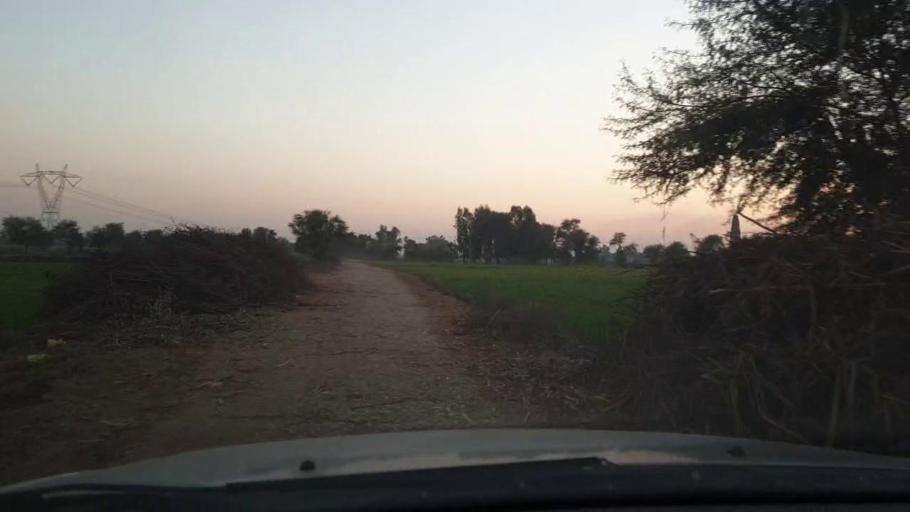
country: PK
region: Sindh
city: Mirpur Mathelo
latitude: 28.0226
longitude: 69.5159
